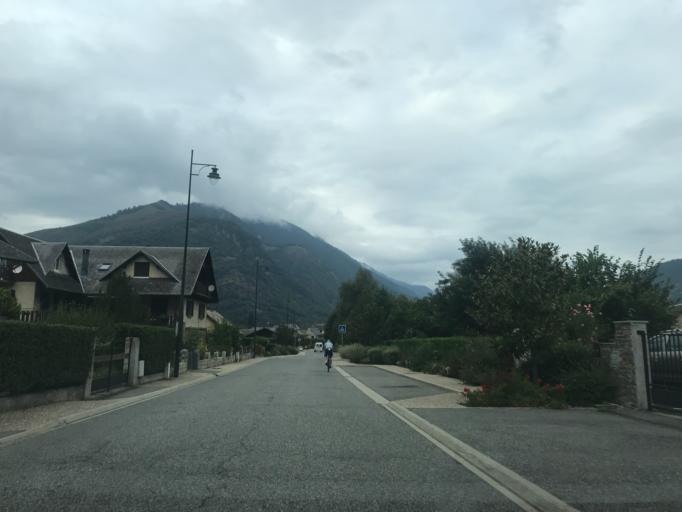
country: FR
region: Midi-Pyrenees
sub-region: Departement de la Haute-Garonne
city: Bagneres-de-Luchon
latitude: 42.7797
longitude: 0.6028
